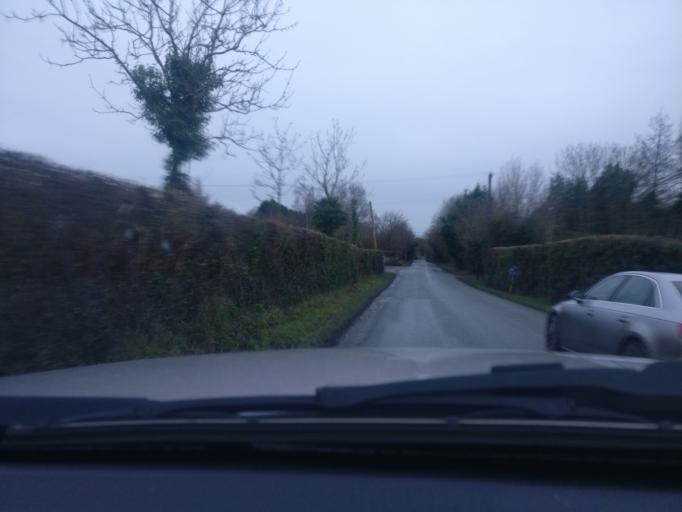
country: IE
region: Leinster
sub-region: Kildare
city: Maynooth
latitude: 53.4475
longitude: -6.6194
